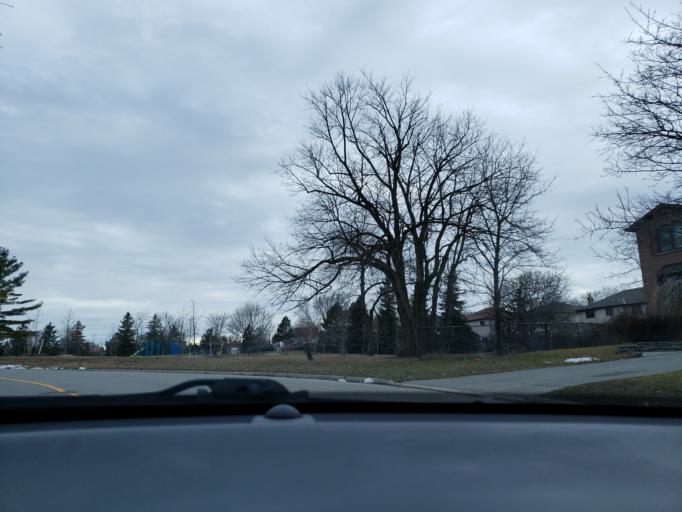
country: CA
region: Ontario
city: Newmarket
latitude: 44.0658
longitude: -79.4759
